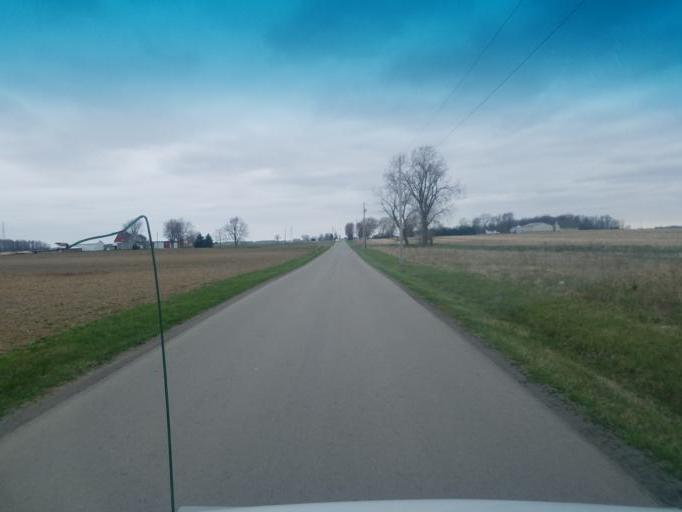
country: US
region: Ohio
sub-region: Allen County
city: Delphos
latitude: 40.9179
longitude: -84.3735
